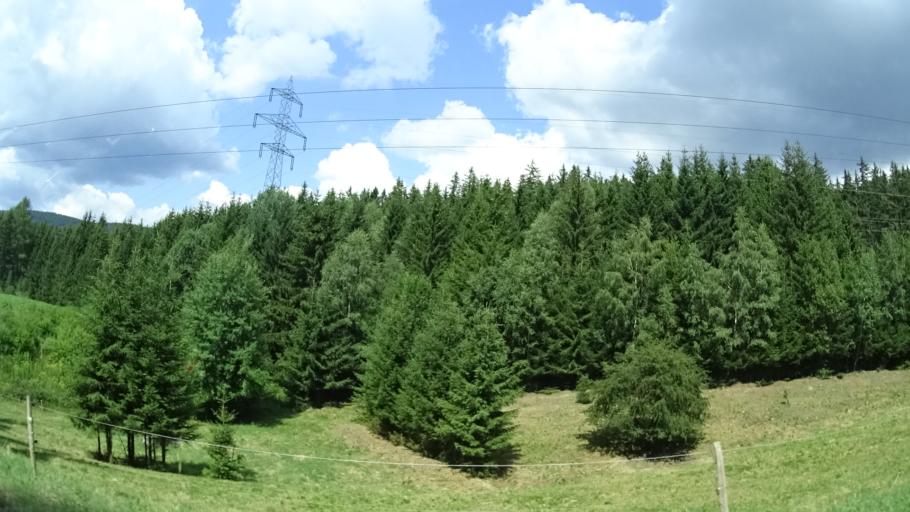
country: DE
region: Thuringia
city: Altenfeld
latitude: 50.5708
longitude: 10.9814
